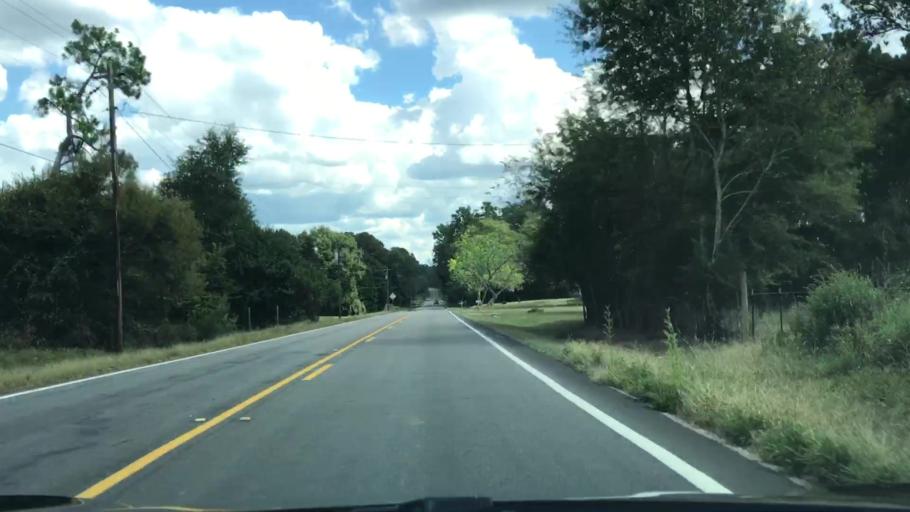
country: US
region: Georgia
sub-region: Greene County
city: Greensboro
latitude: 33.5649
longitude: -83.1467
